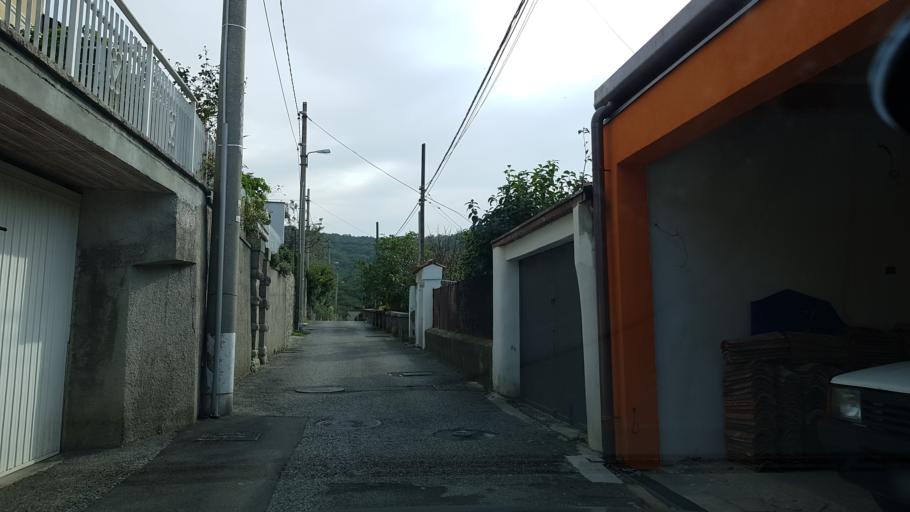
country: IT
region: Friuli Venezia Giulia
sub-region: Provincia di Trieste
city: Trieste
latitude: 45.6509
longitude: 13.8095
